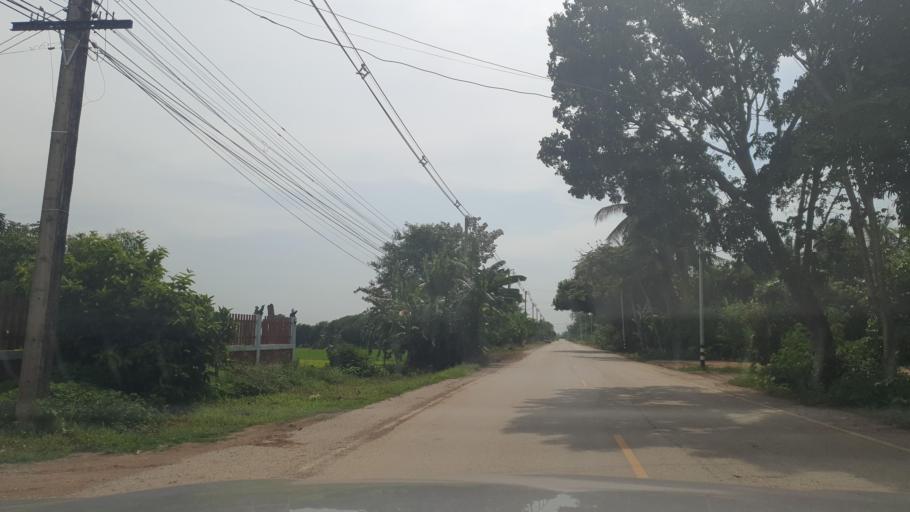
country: TH
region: Sukhothai
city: Si Samrong
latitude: 17.1388
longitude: 99.8483
